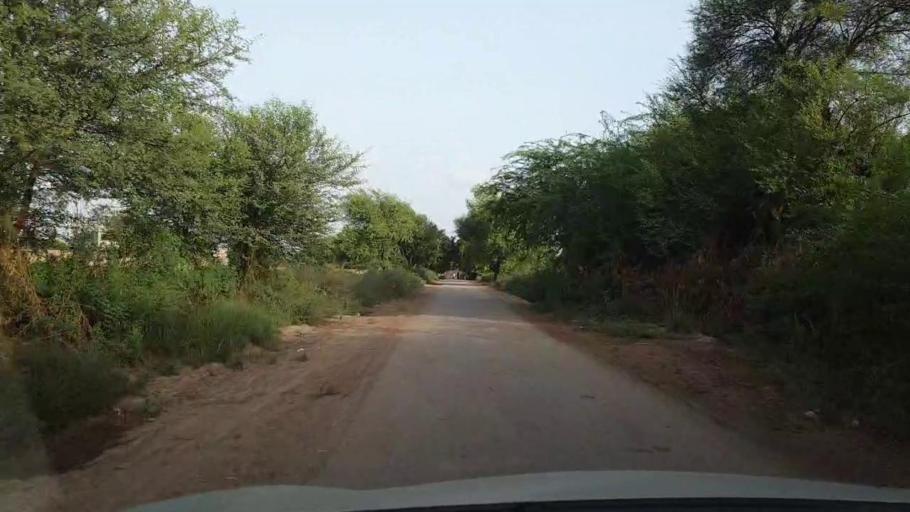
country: PK
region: Sindh
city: Tando Ghulam Ali
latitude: 25.0965
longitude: 68.8887
